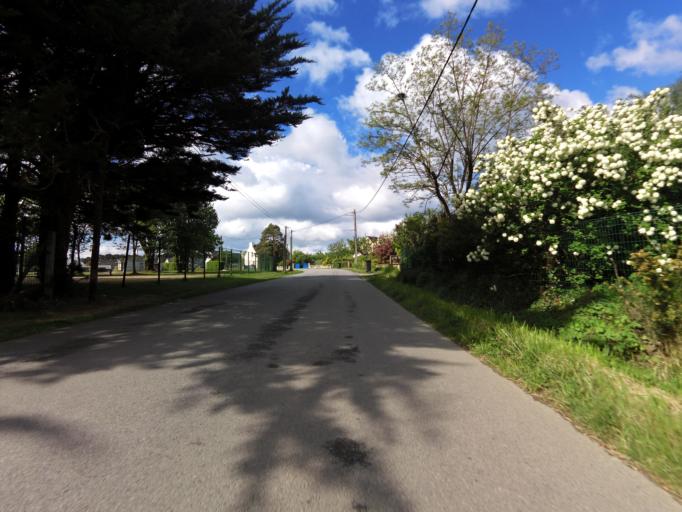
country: FR
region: Brittany
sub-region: Departement du Morbihan
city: Baden
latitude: 47.6260
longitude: -2.8982
